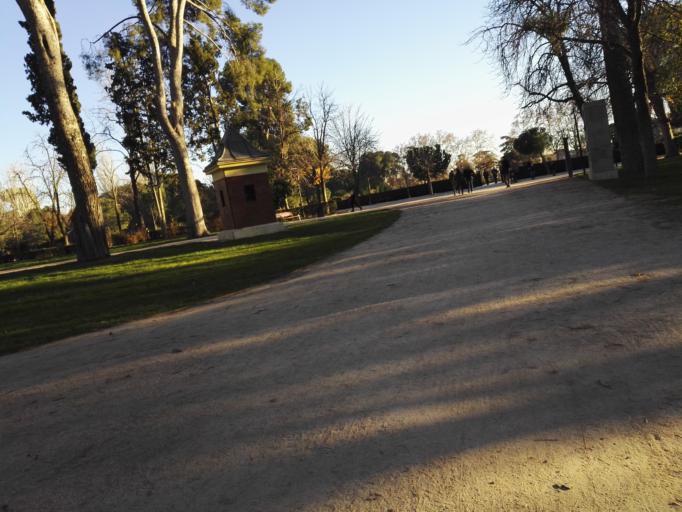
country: ES
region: Madrid
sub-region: Provincia de Madrid
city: Retiro
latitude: 40.4119
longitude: -3.6807
